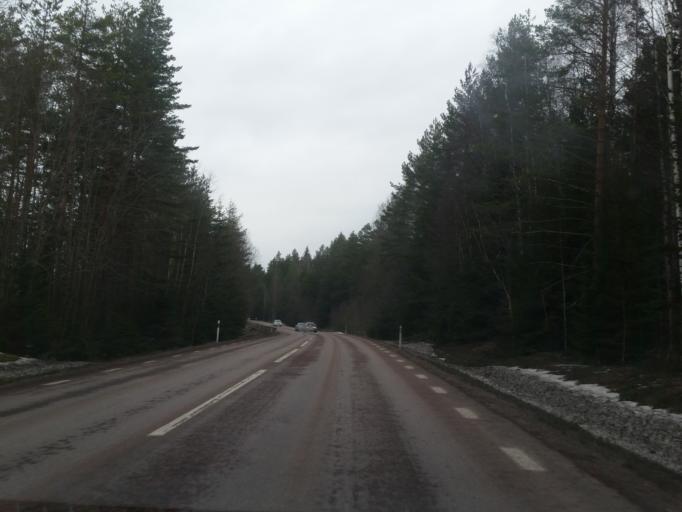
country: SE
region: Dalarna
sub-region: Mora Kommun
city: Mora
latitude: 61.0820
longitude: 14.3300
